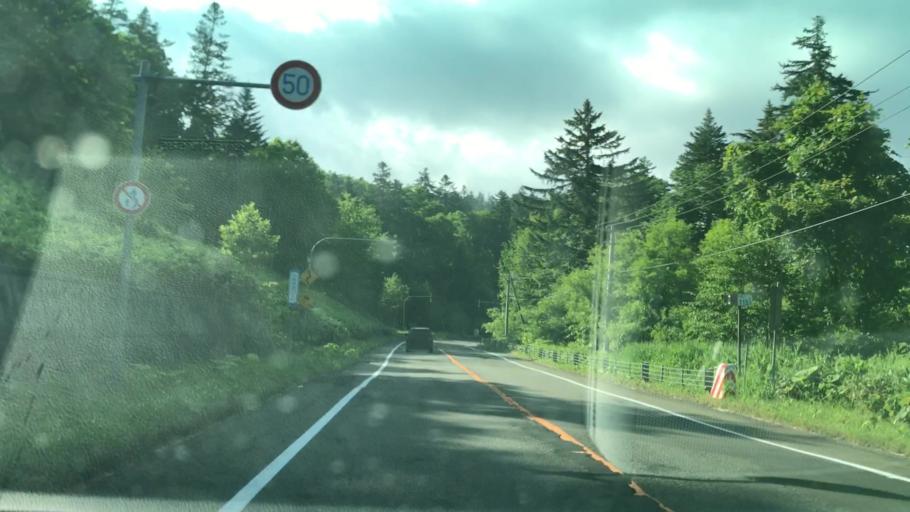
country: JP
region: Hokkaido
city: Shimo-furano
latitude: 42.9095
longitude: 142.4127
